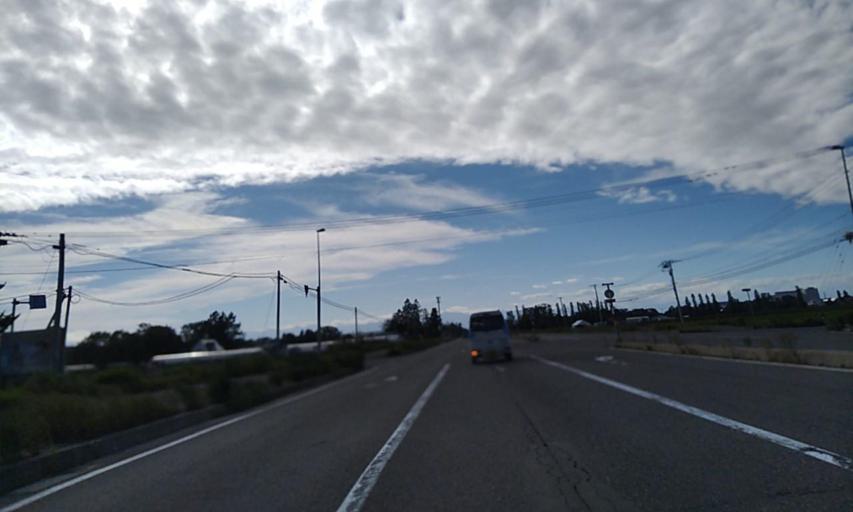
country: JP
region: Hokkaido
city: Obihiro
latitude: 42.9172
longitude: 143.2819
